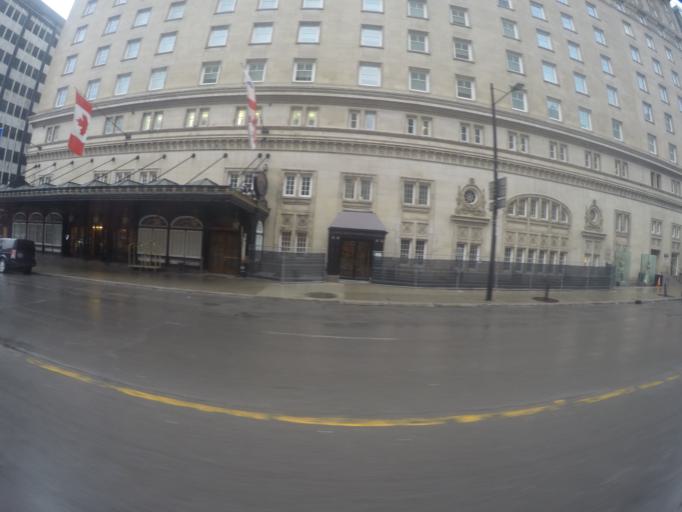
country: CA
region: Quebec
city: Montreal-Ouest
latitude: 45.4156
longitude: -73.6543
